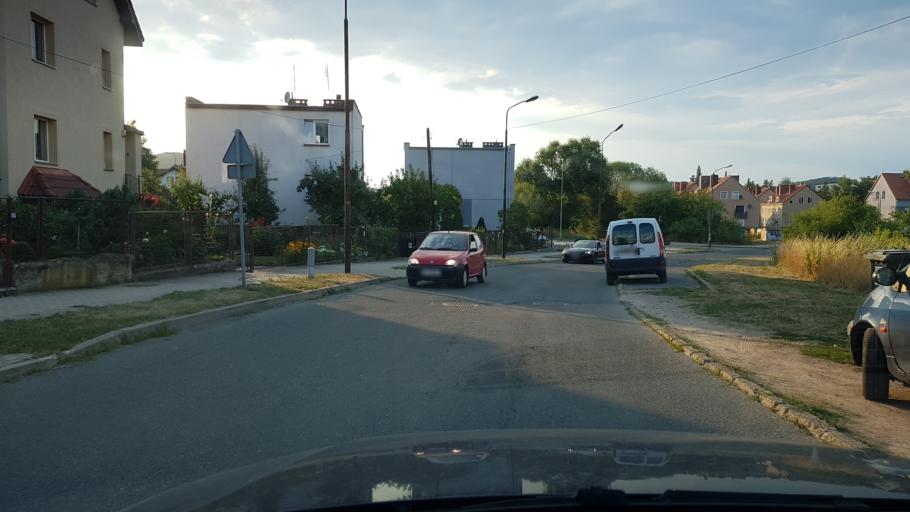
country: PL
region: Lower Silesian Voivodeship
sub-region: Jelenia Gora
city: Jelenia Gora
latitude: 50.8876
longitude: 15.7309
